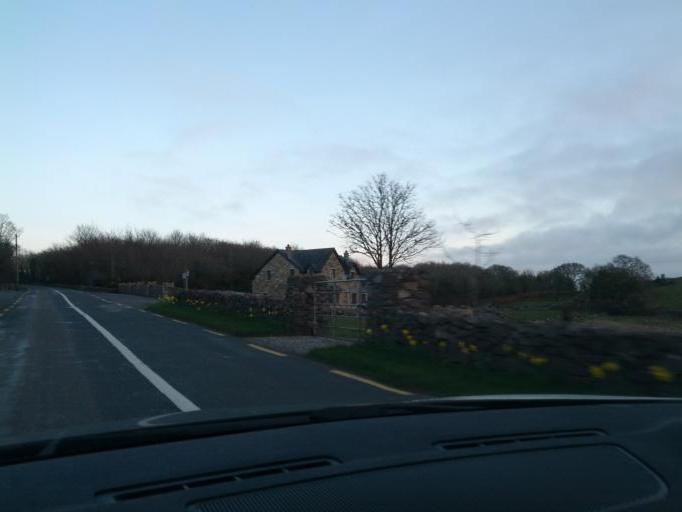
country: IE
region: Connaught
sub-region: Sligo
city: Ballymote
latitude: 53.9744
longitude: -8.4492
